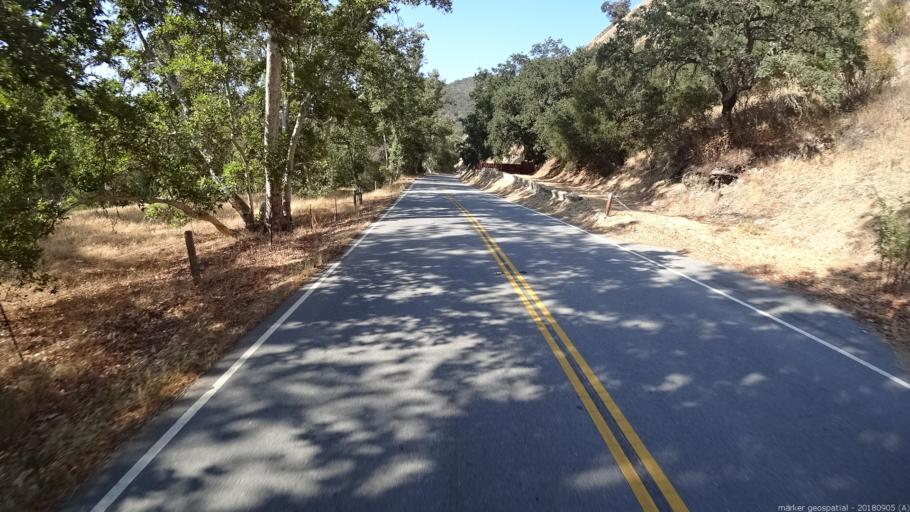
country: US
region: California
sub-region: Monterey County
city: Greenfield
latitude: 36.2568
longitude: -121.4306
